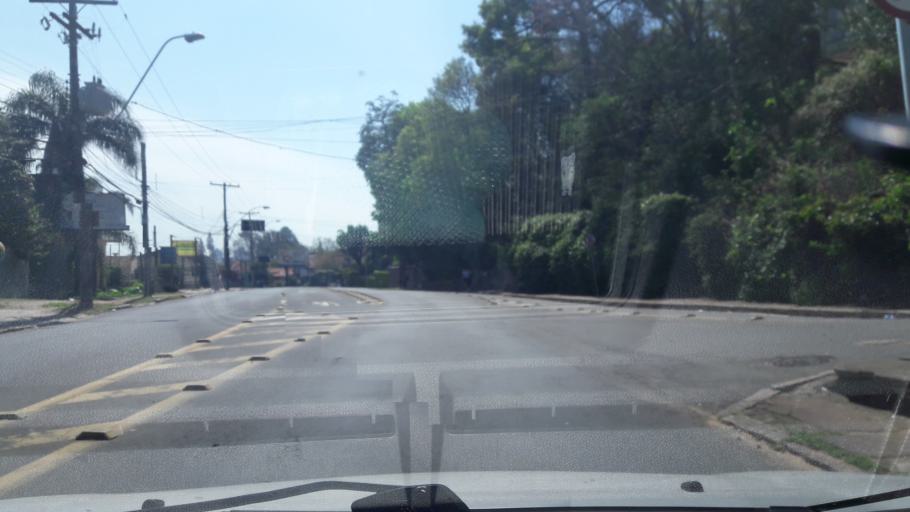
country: BR
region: Rio Grande do Sul
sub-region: Guaiba
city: Guaiba
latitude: -30.1188
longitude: -51.2533
